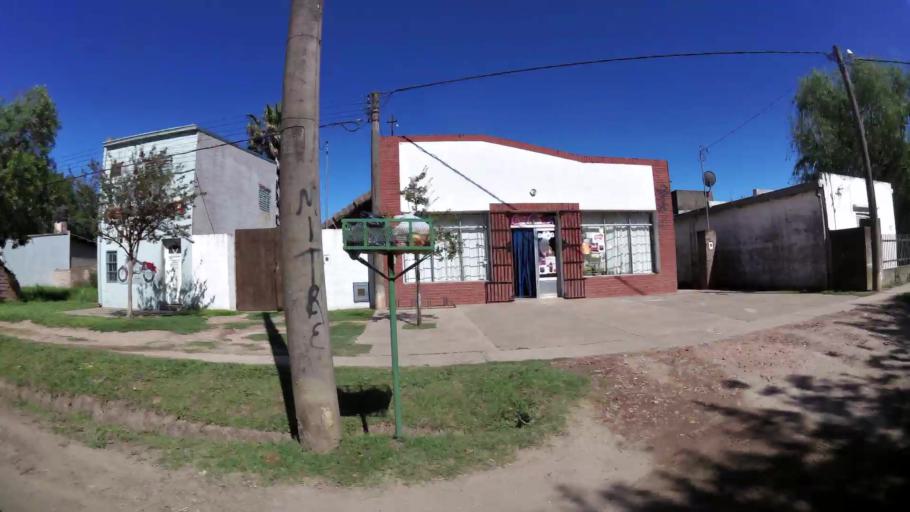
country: AR
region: Santa Fe
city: Esperanza
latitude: -31.4667
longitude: -60.9379
